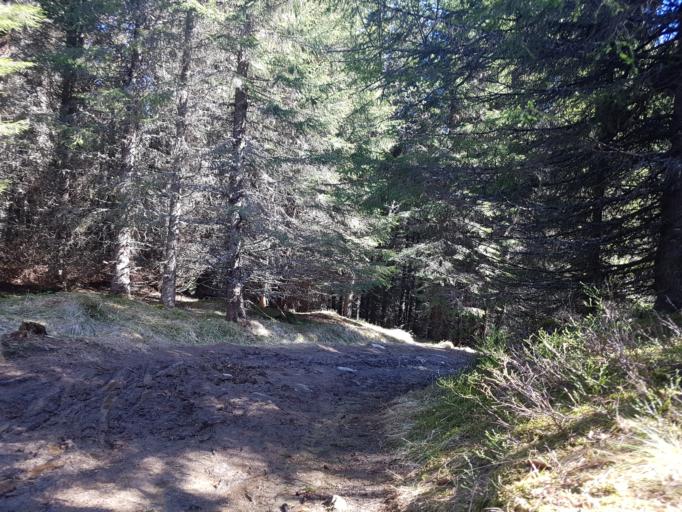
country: NO
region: Sor-Trondelag
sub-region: Trondheim
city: Trondheim
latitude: 63.4243
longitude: 10.3161
